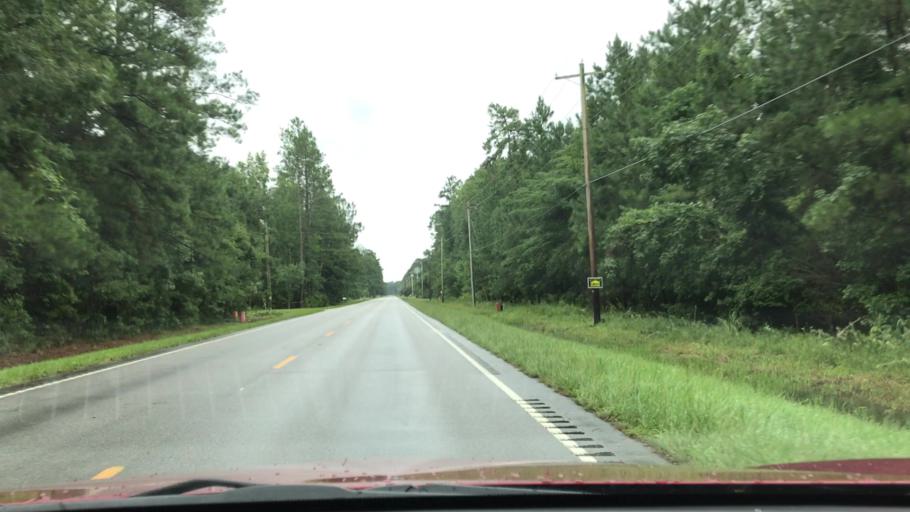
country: US
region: South Carolina
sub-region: Horry County
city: Conway
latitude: 33.7841
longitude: -79.0750
